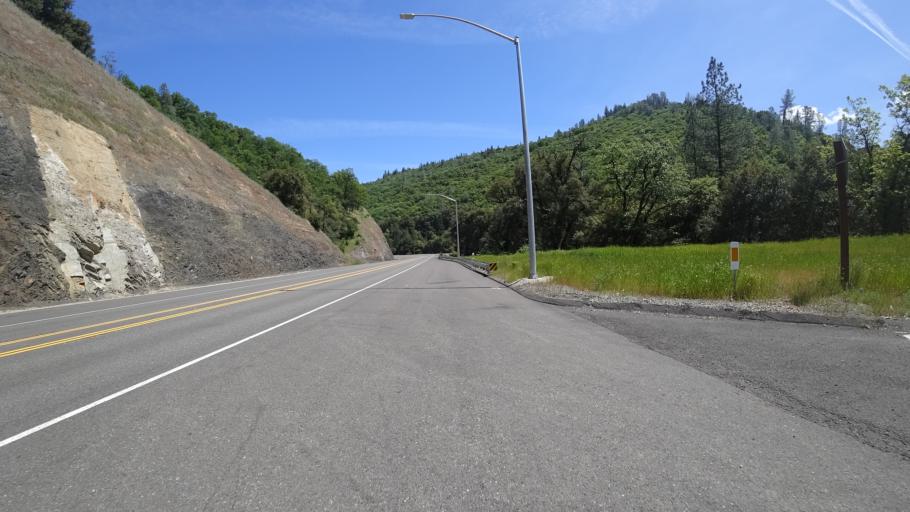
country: US
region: California
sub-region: Trinity County
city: Lewiston
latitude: 40.6693
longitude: -122.6888
